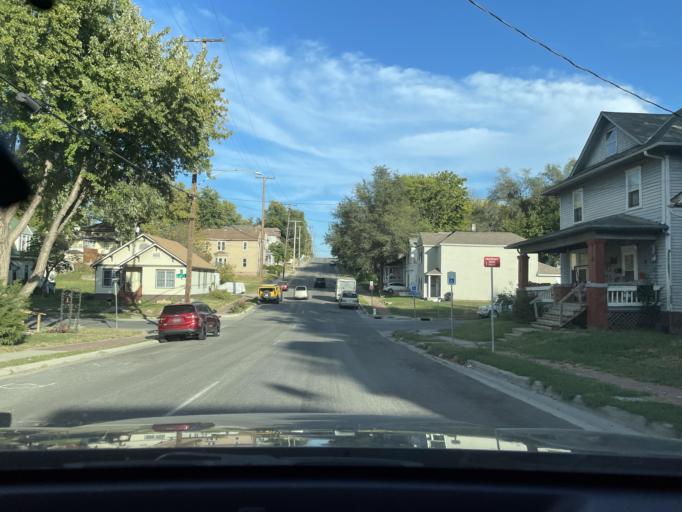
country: US
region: Missouri
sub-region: Buchanan County
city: Saint Joseph
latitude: 39.7683
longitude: -94.8417
